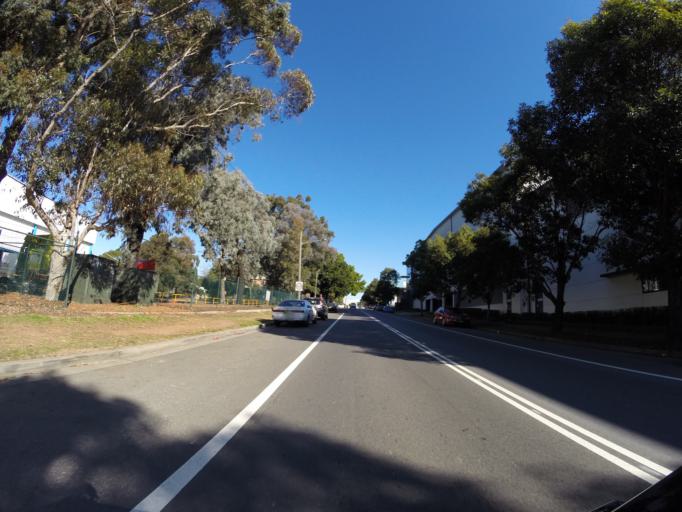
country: AU
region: New South Wales
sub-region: Auburn
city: Lidcombe
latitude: -33.8579
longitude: 151.0595
